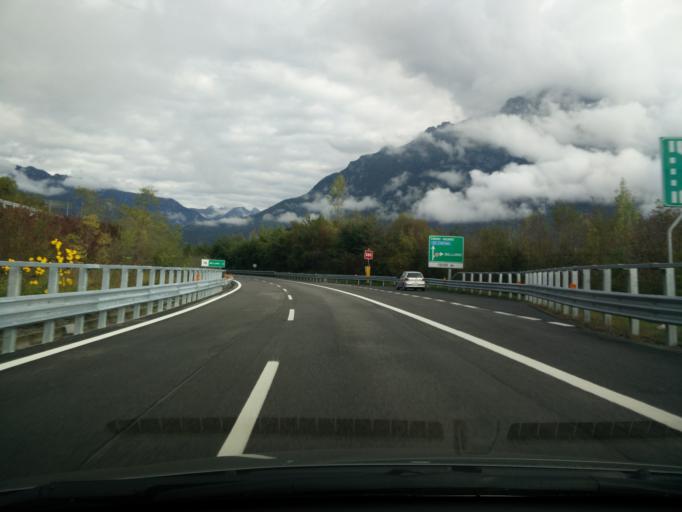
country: IT
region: Veneto
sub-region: Provincia di Belluno
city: Soccher-Paiane-Casan-Arsie
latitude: 46.1538
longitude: 12.3183
